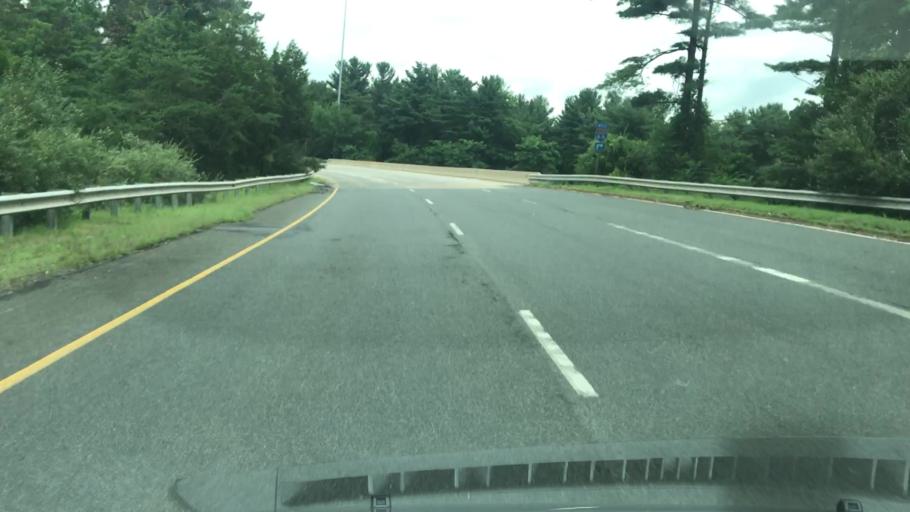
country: US
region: Virginia
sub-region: City of Fairfax
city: Fairfax
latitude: 38.8619
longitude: -77.3438
